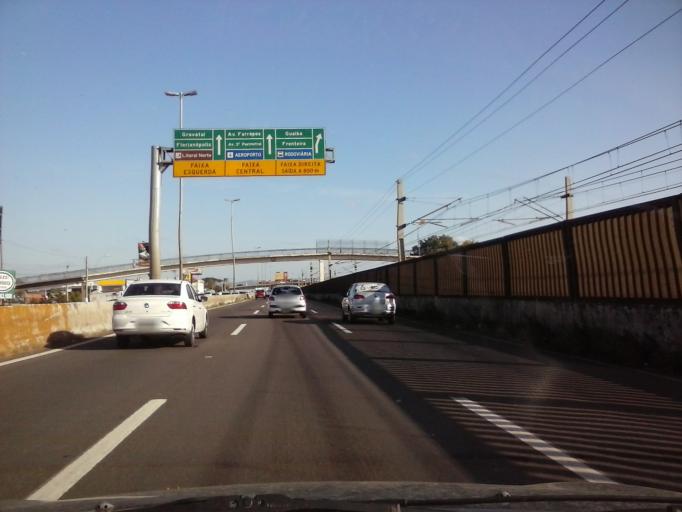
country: BR
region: Rio Grande do Sul
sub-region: Canoas
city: Canoas
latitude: -29.9584
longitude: -51.1762
